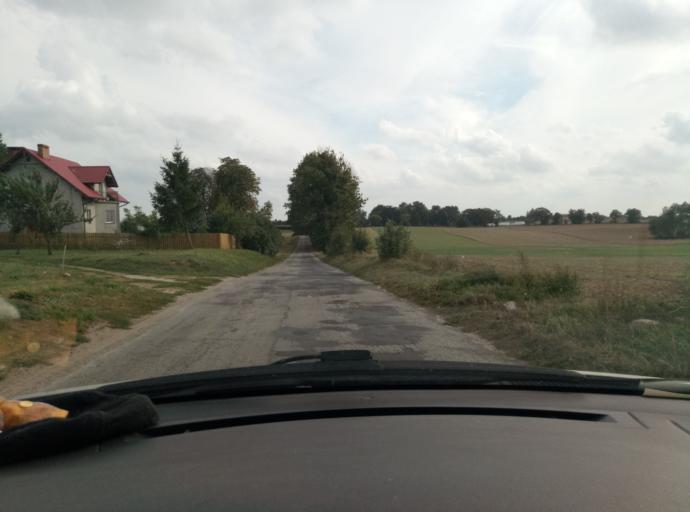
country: PL
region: Kujawsko-Pomorskie
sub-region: Powiat brodnicki
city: Jablonowo Pomorskie
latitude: 53.3785
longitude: 19.2450
